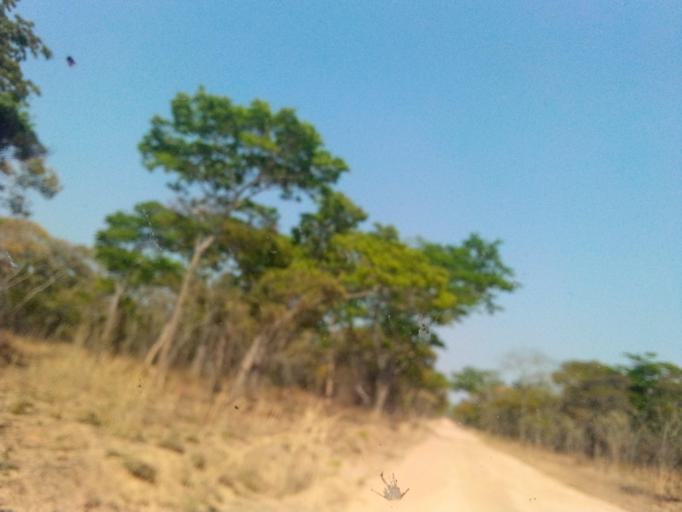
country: ZM
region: Northern
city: Mpika
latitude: -12.2419
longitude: 30.8588
